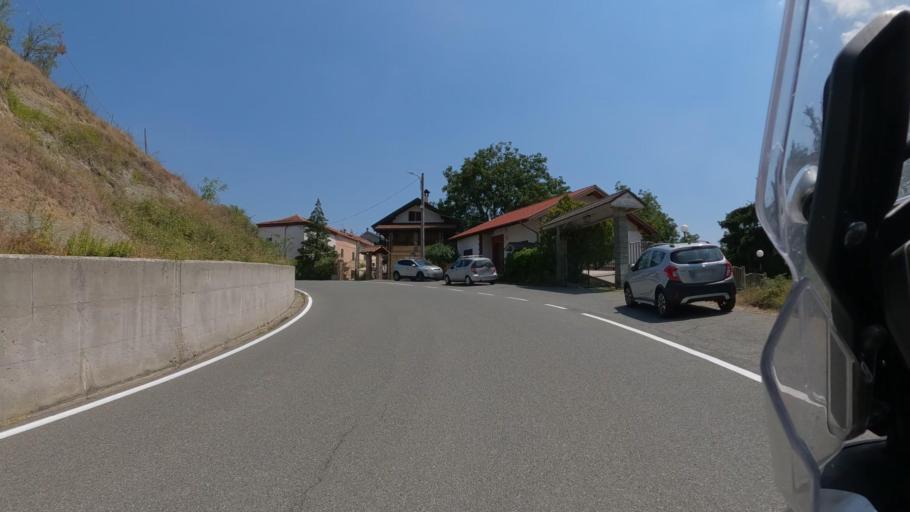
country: IT
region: Piedmont
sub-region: Provincia di Alessandria
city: Cassinelle-Concentrico
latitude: 44.5783
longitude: 8.5431
